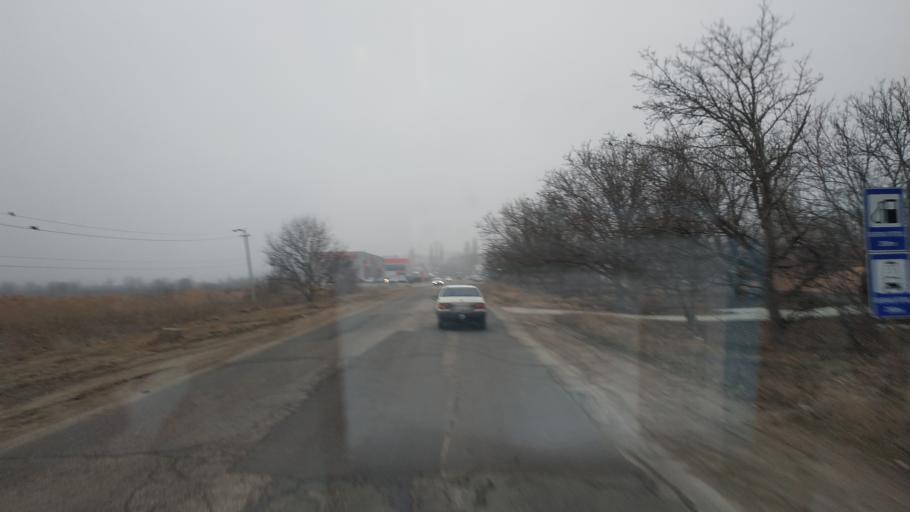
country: MD
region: Laloveni
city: Ialoveni
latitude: 46.9486
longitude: 28.7688
